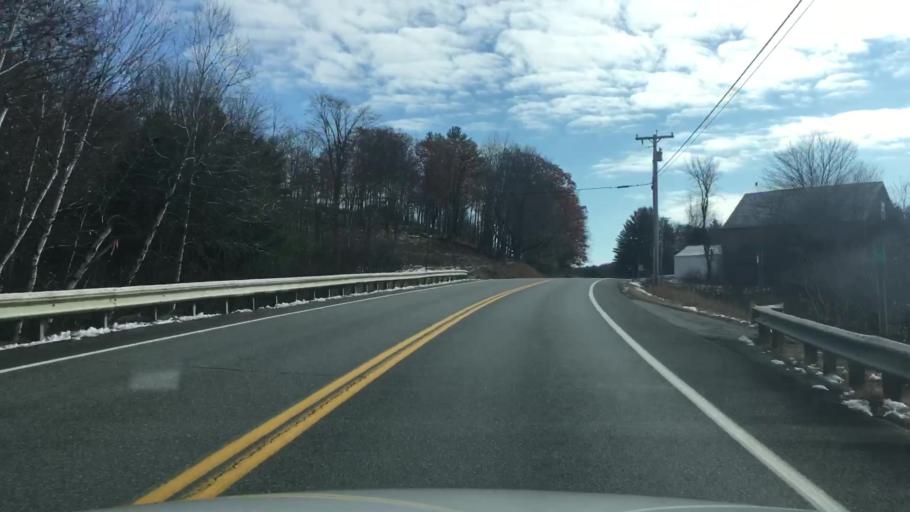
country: US
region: Maine
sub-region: Kennebec County
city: Wayne
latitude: 44.3376
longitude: -70.0166
